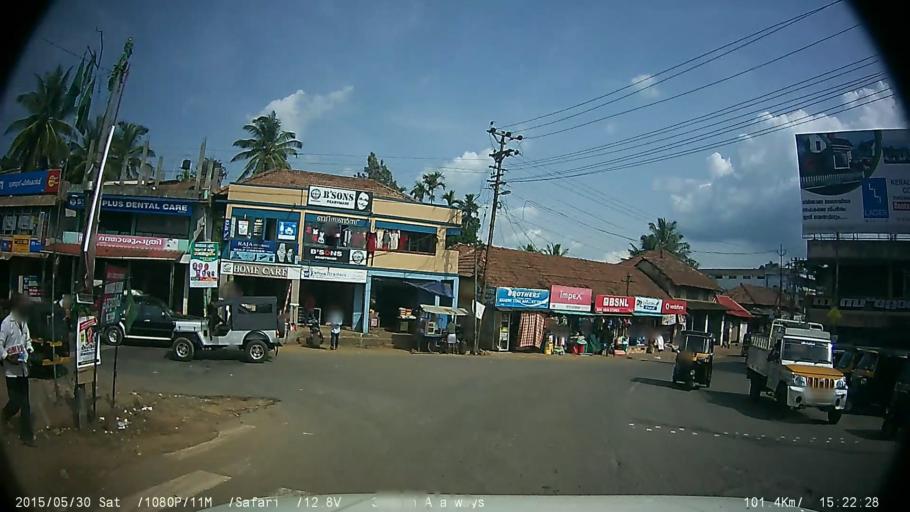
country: IN
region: Kerala
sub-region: Wayanad
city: Panamaram
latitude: 11.7407
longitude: 76.0734
